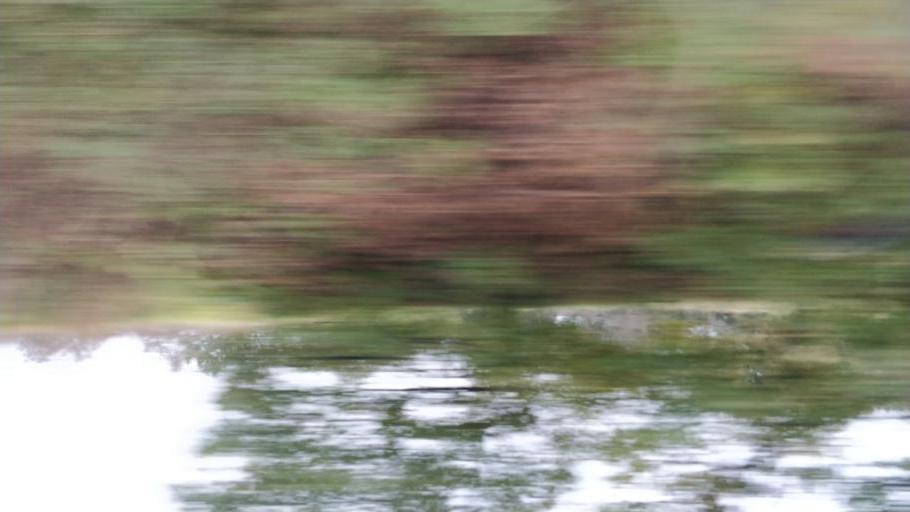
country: GB
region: England
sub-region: Borough of Wigan
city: Hindley
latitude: 53.5437
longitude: -2.5581
